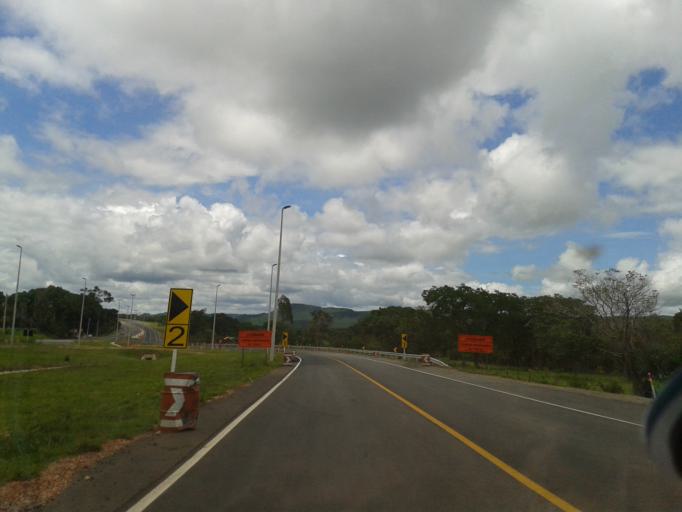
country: BR
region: Goias
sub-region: Goias
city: Goias
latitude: -15.9874
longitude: -50.0766
